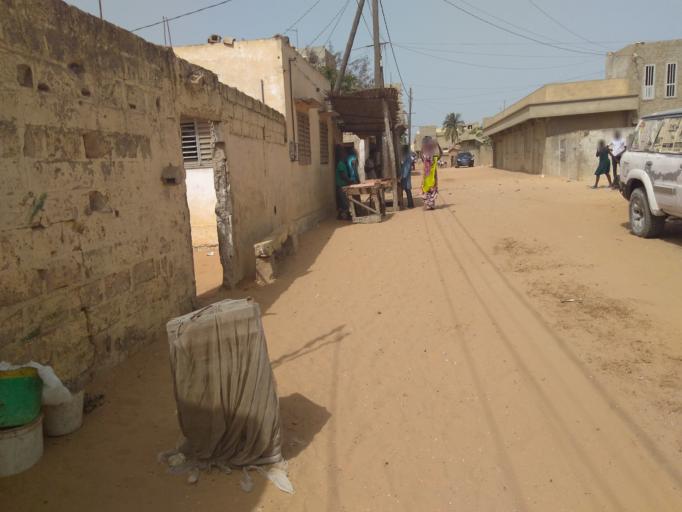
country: SN
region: Dakar
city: Pikine
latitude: 14.7928
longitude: -17.3370
